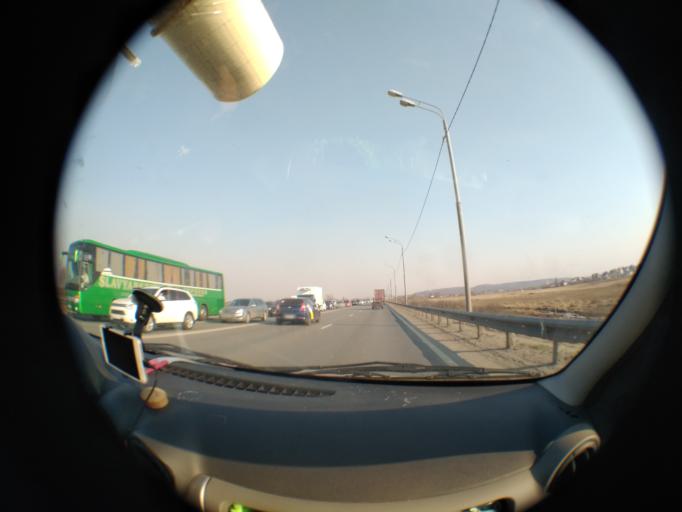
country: RU
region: Moskovskaya
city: Ostrovtsy
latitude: 55.5800
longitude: 38.0179
